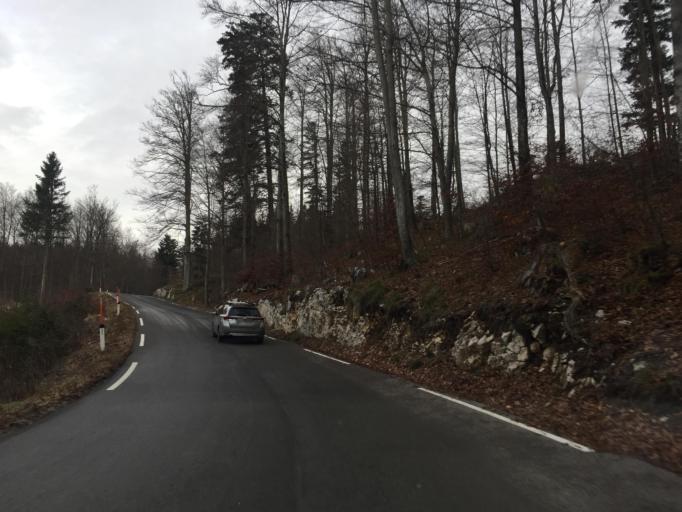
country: SI
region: Nova Gorica
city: Sempas
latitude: 45.9982
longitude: 13.7795
